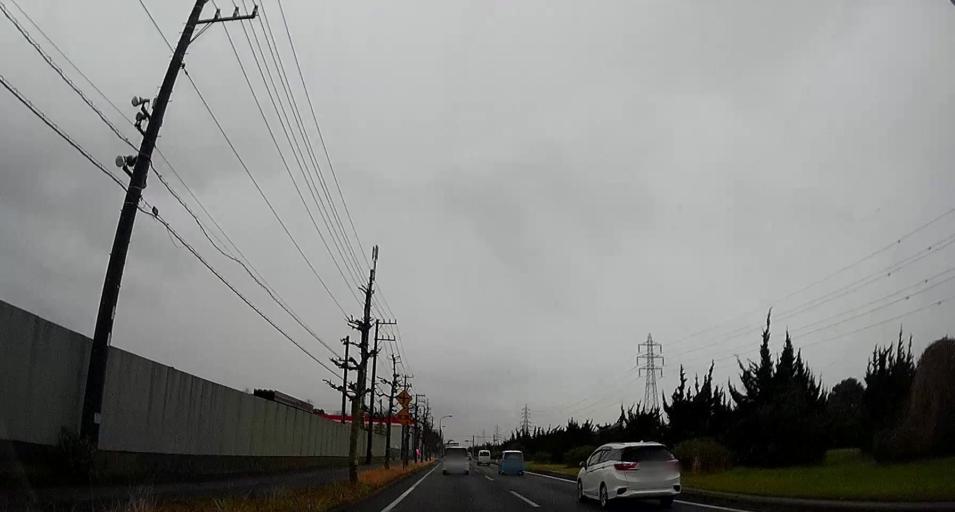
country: JP
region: Chiba
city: Ichihara
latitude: 35.5133
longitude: 140.0575
